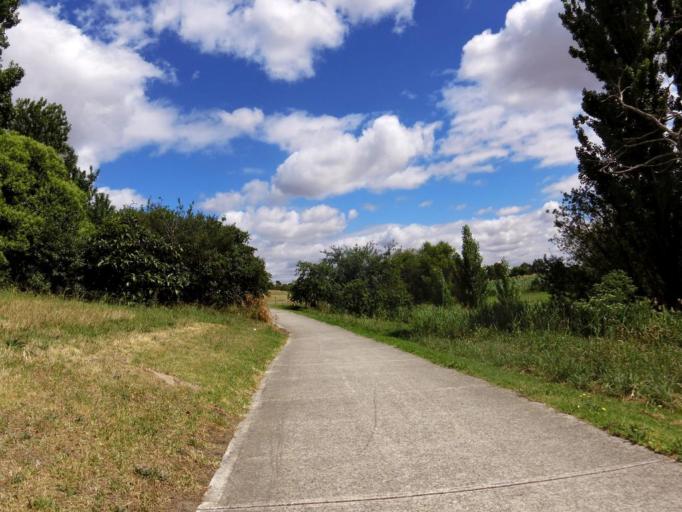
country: AU
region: Victoria
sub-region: Banyule
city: Bundoora
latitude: -37.6896
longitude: 145.0528
